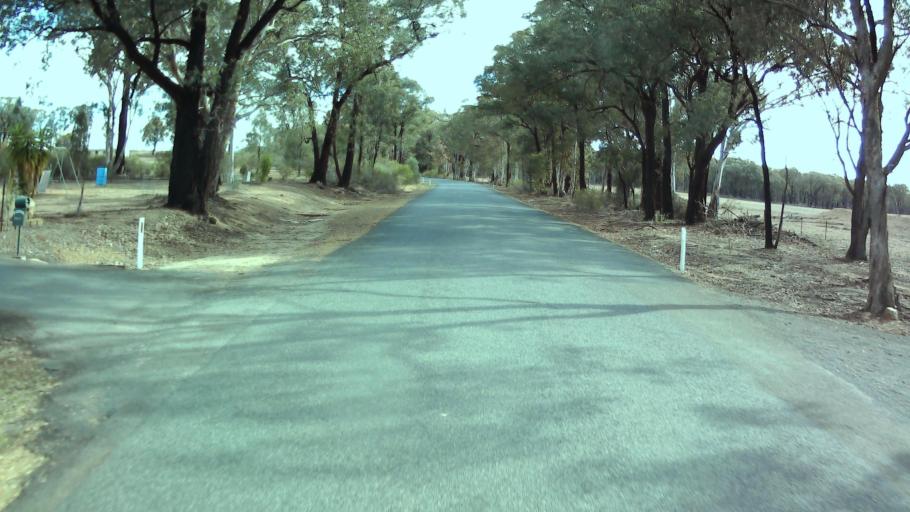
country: AU
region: New South Wales
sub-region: Weddin
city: Grenfell
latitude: -33.8818
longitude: 148.2001
